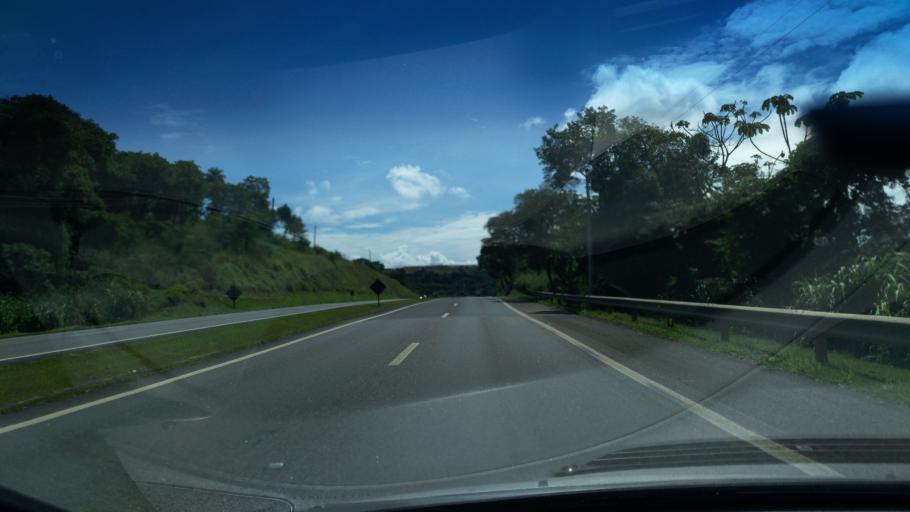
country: BR
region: Sao Paulo
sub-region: Santo Antonio Do Jardim
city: Espirito Santo do Pinhal
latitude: -22.2165
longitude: -46.7857
